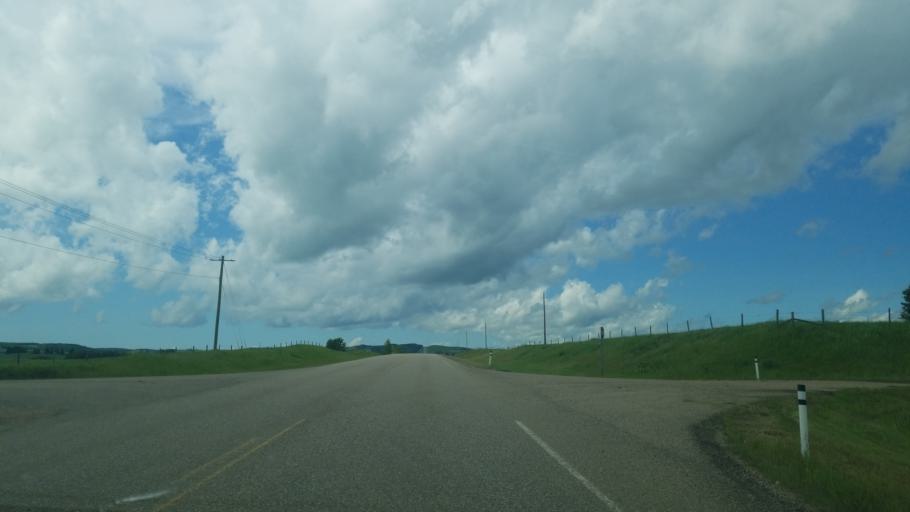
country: CA
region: Saskatchewan
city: Lloydminster
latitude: 53.1617
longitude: -110.1757
